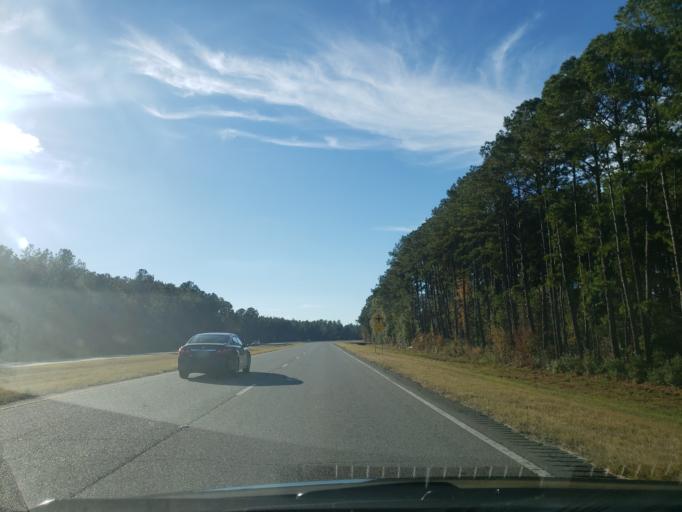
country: US
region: Georgia
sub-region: Ware County
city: Deenwood
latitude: 31.2095
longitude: -82.4076
